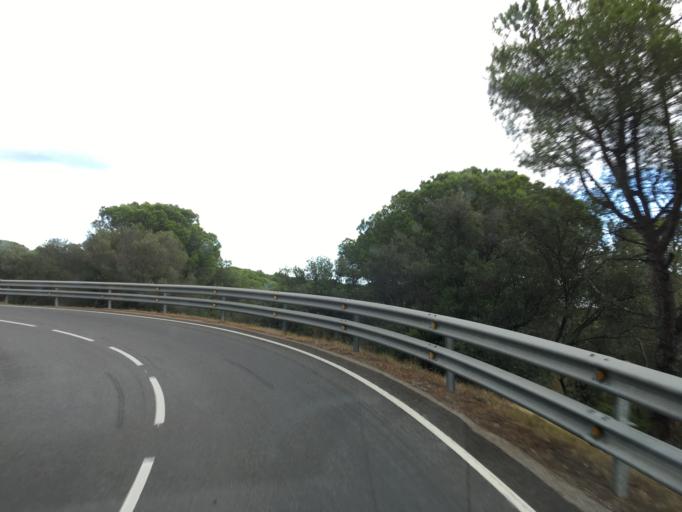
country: ES
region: Catalonia
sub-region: Provincia de Girona
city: Llanca
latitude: 42.3432
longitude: 3.1831
